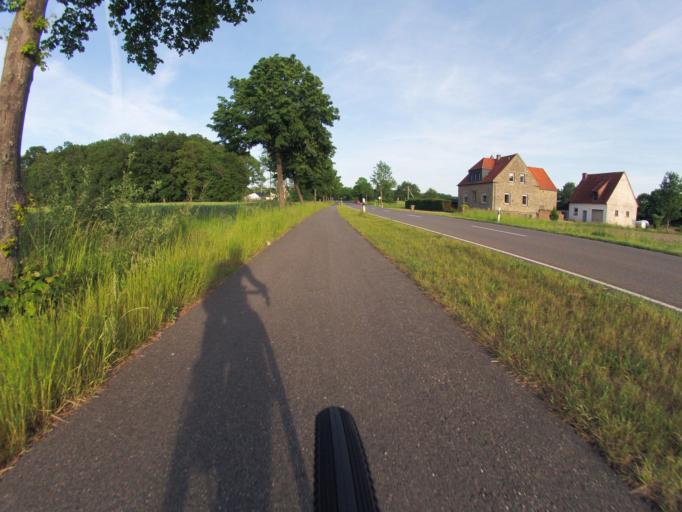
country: DE
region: North Rhine-Westphalia
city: Ibbenburen
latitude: 52.2614
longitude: 7.7567
